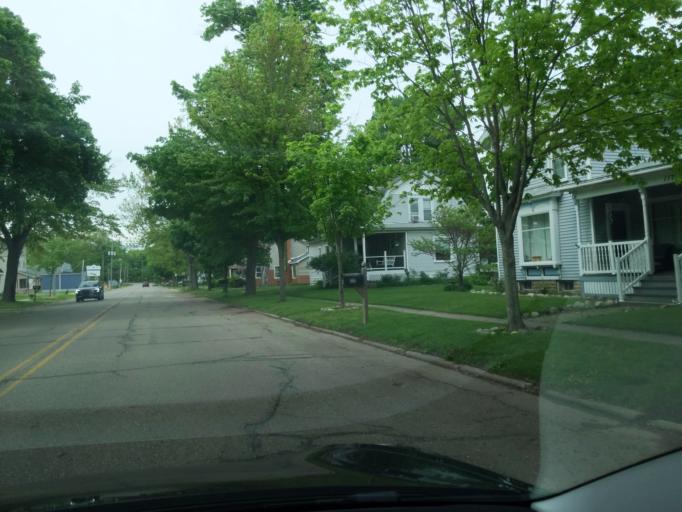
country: US
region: Michigan
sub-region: Ingham County
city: Leslie
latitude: 42.4521
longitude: -84.4319
